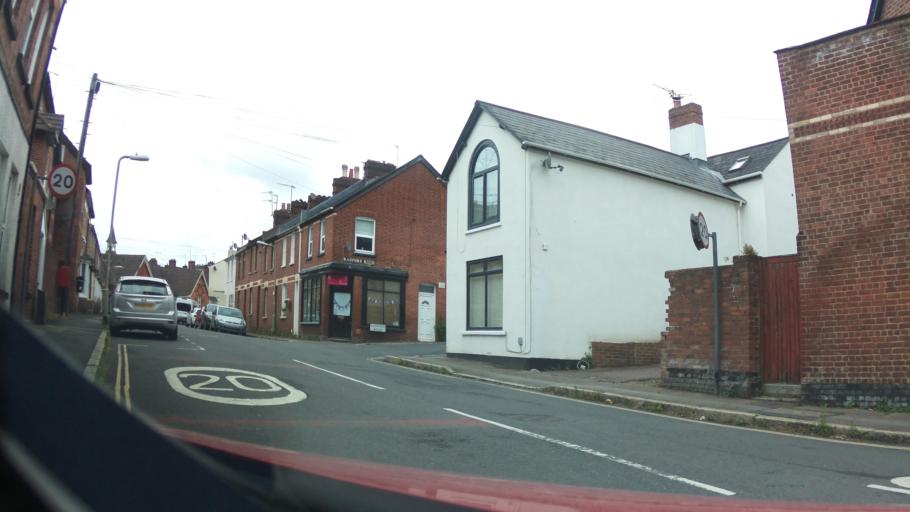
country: GB
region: England
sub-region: Devon
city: Exeter
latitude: 50.7182
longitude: -3.5257
